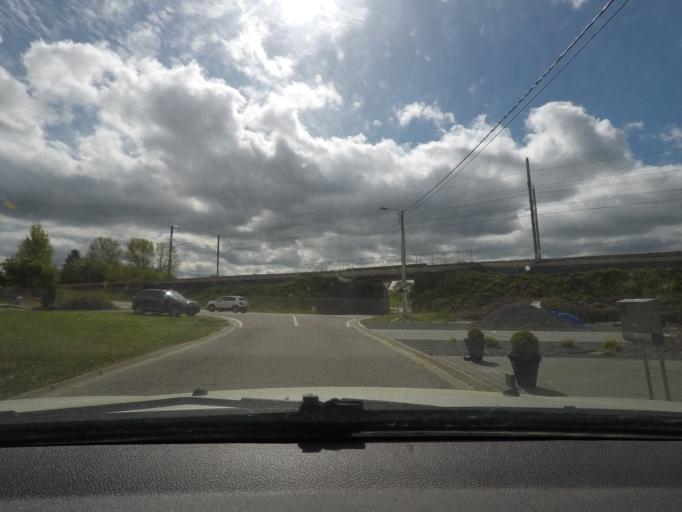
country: BE
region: Wallonia
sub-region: Province du Luxembourg
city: Habay-la-Vieille
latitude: 49.7206
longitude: 5.6160
